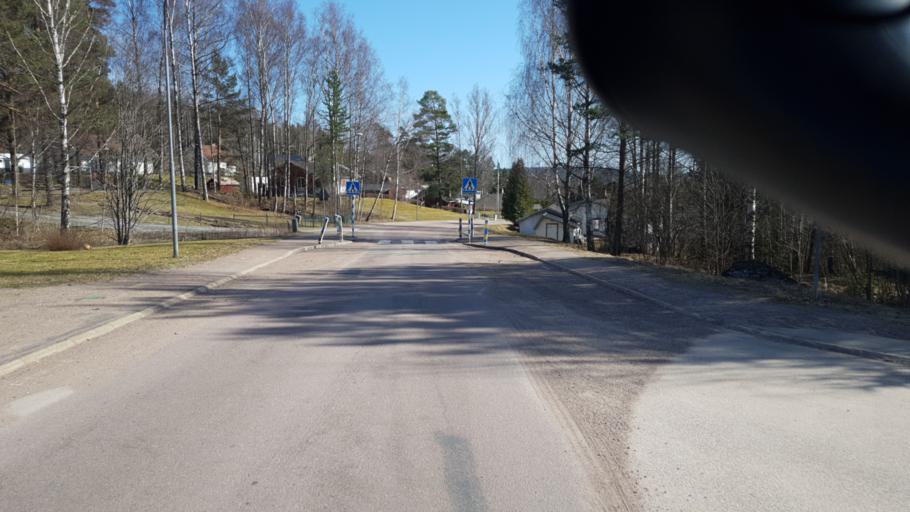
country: SE
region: Vaermland
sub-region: Arvika Kommun
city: Arvika
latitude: 59.6354
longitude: 12.8183
